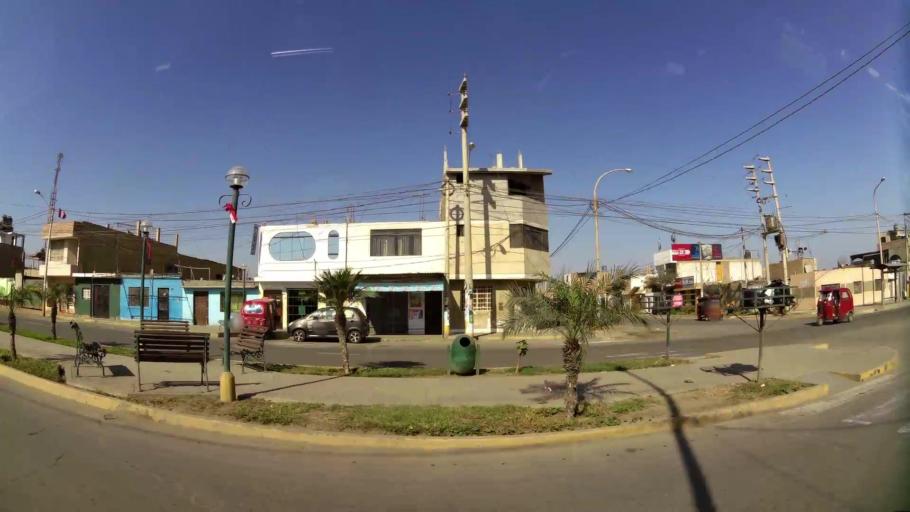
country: PE
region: Ica
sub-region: Provincia de Chincha
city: Chincha Alta
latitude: -13.3989
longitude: -76.1283
